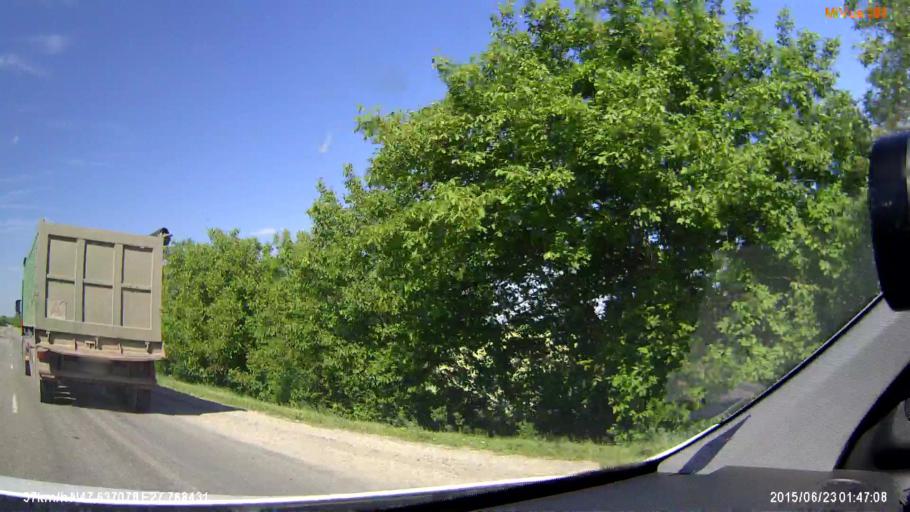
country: MD
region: Falesti
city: Falesti
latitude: 47.6370
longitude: 27.7683
